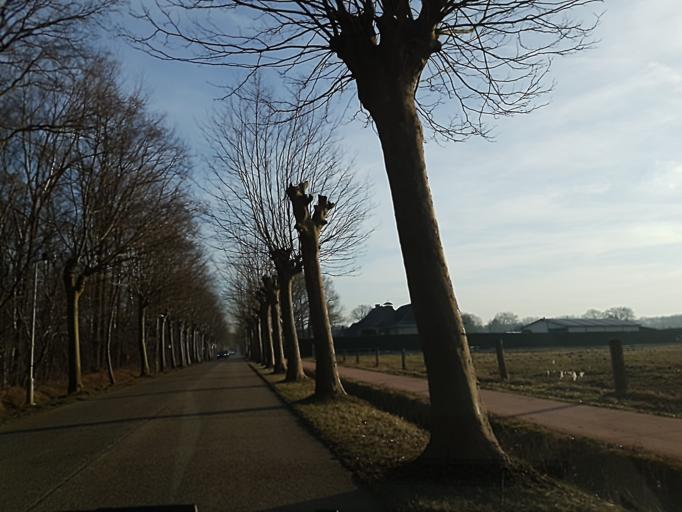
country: BE
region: Flanders
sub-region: Provincie Antwerpen
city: Schilde
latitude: 51.2527
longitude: 4.6020
